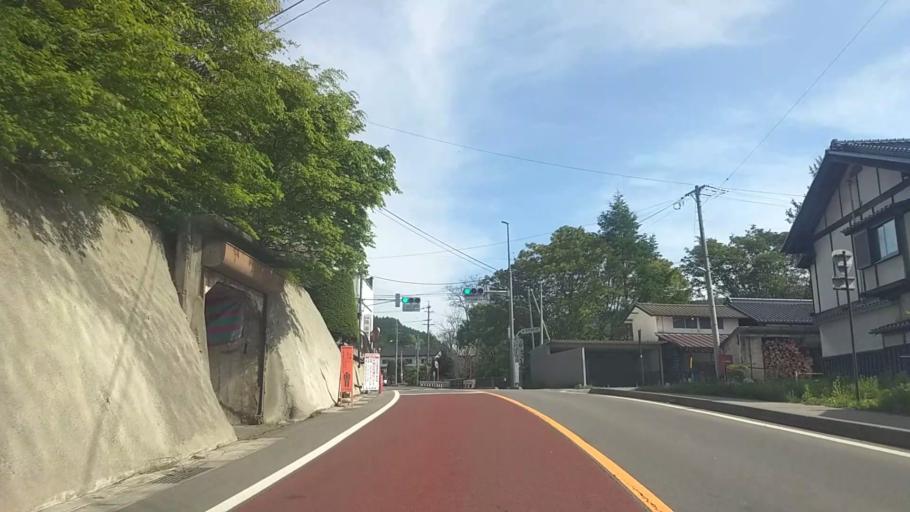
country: JP
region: Nagano
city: Saku
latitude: 36.0411
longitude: 138.4715
